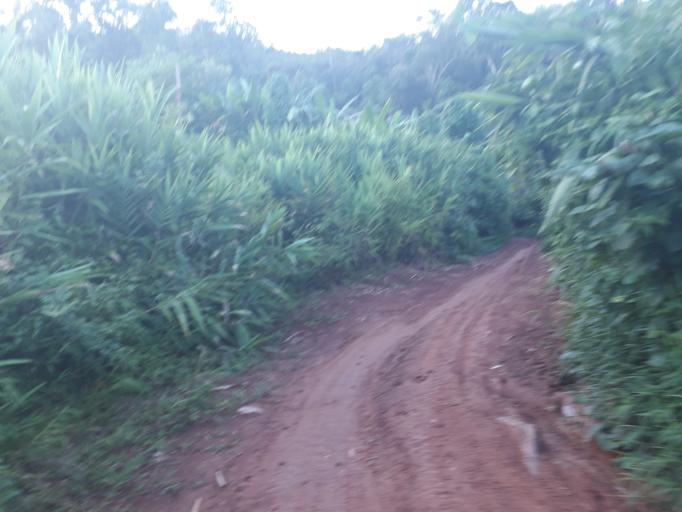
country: CN
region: Yunnan
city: Menglie
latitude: 22.1242
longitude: 101.7568
